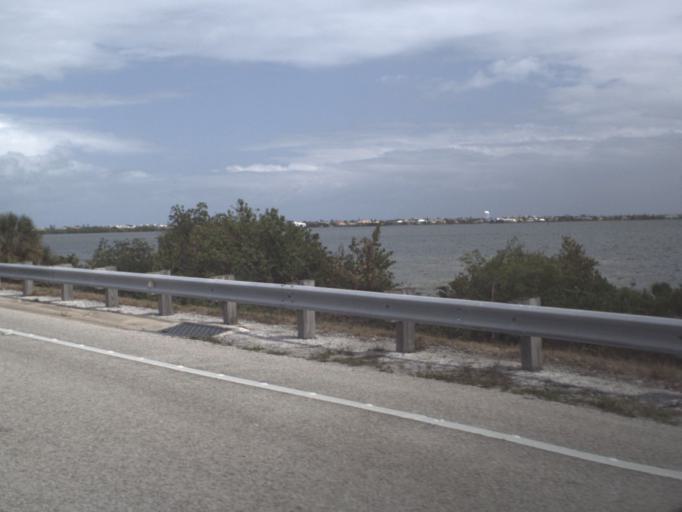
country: US
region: Florida
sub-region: Brevard County
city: South Patrick Shores
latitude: 28.2087
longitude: -80.6352
